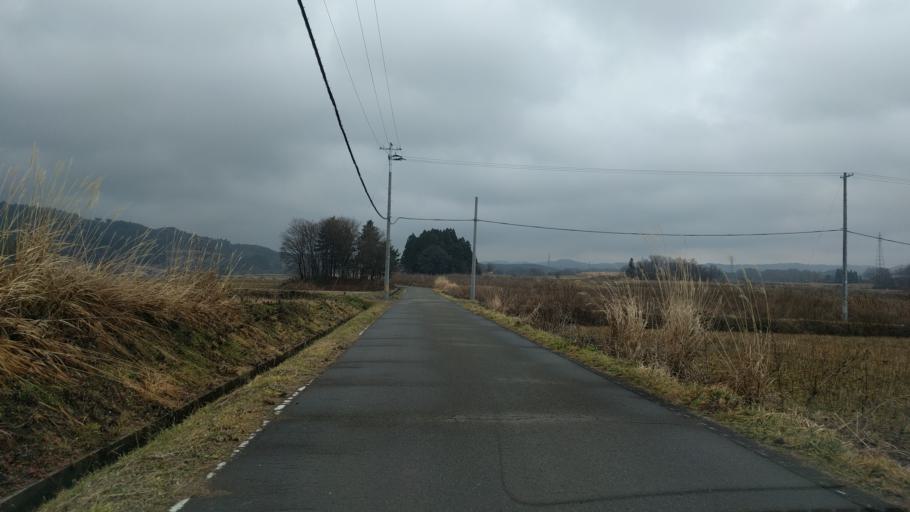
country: JP
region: Fukushima
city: Kitakata
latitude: 37.5713
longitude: 139.9536
